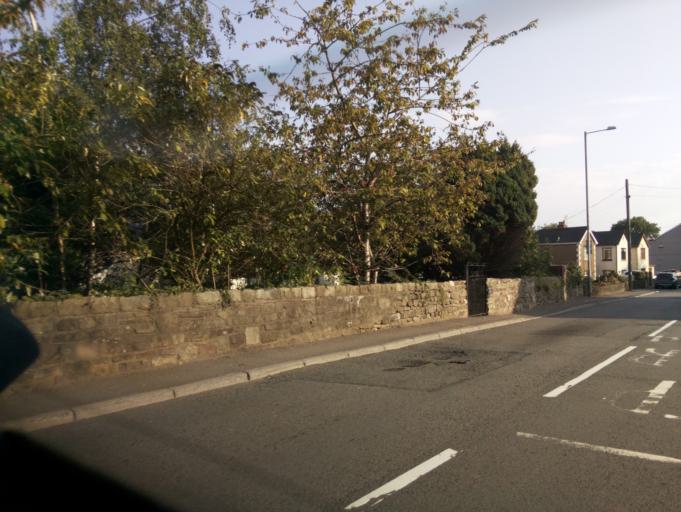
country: GB
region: Wales
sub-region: Torfaen County Borough
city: Pontypool
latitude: 51.6929
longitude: -3.0285
